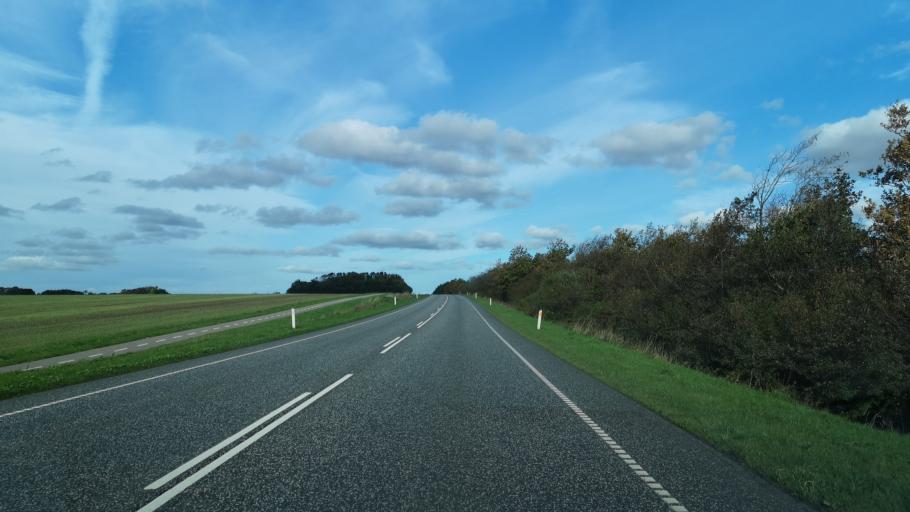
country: DK
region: Central Jutland
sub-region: Holstebro Kommune
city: Holstebro
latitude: 56.3211
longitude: 8.6088
